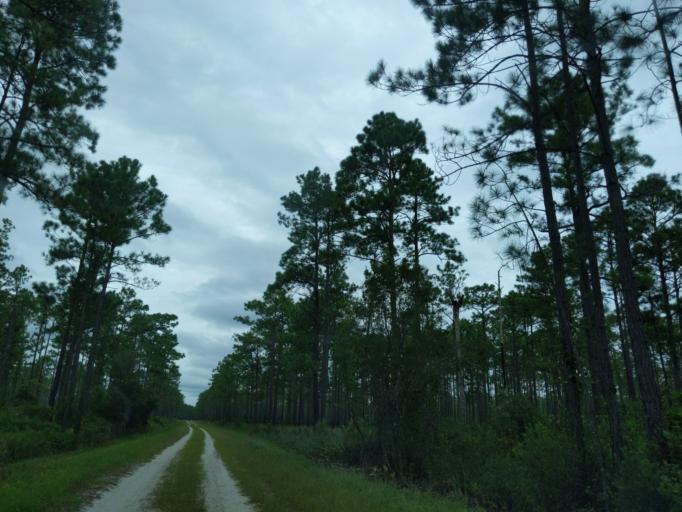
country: US
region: Florida
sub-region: Gadsden County
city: Midway
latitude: 30.3704
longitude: -84.4731
